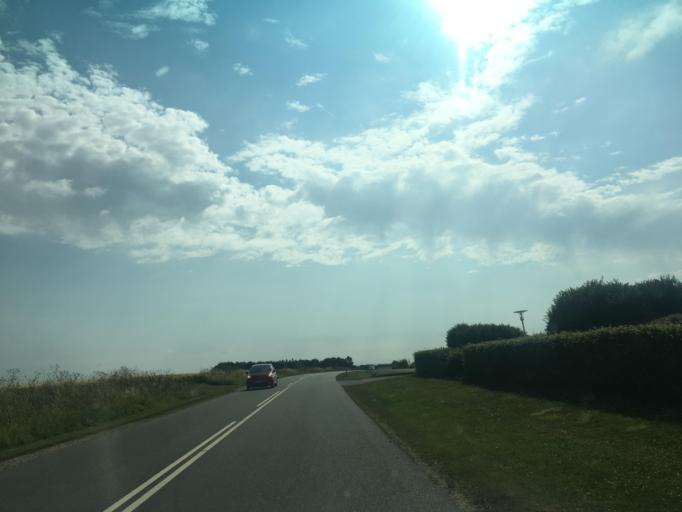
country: DK
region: North Denmark
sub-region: Thisted Kommune
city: Thisted
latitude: 56.8355
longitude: 8.5726
